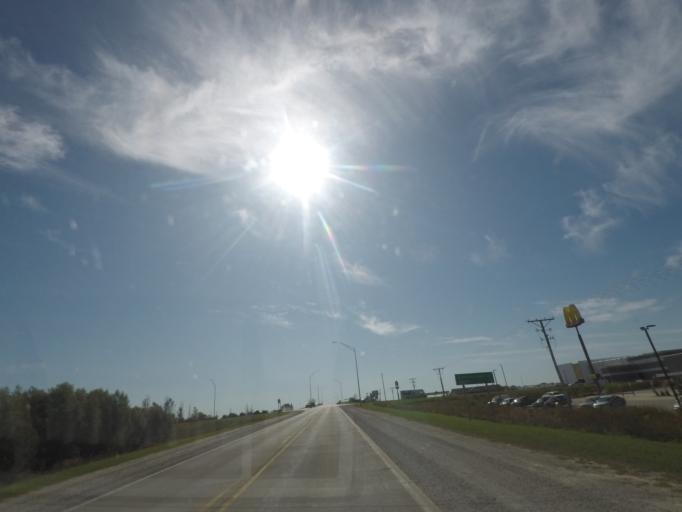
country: US
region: Iowa
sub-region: Story County
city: Nevada
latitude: 42.0110
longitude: -93.4349
